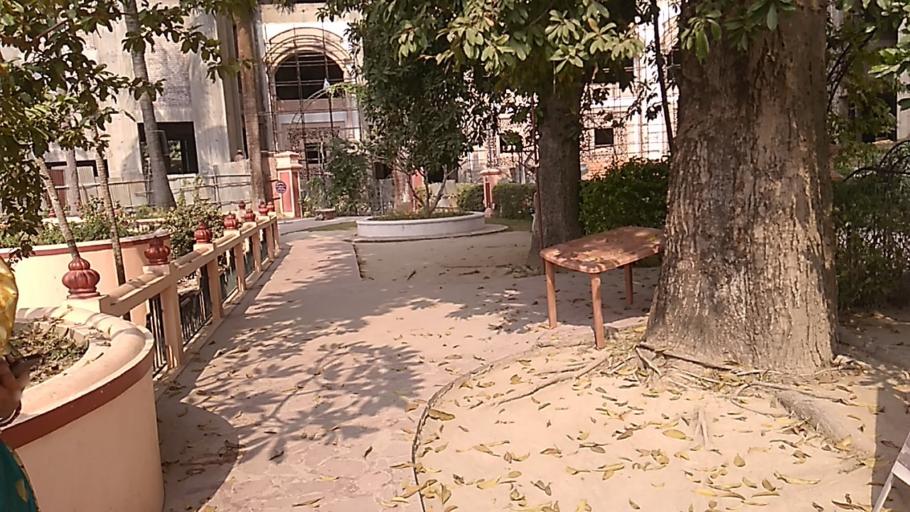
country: IN
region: West Bengal
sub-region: Nadia
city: Navadwip
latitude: 23.4242
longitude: 88.3885
